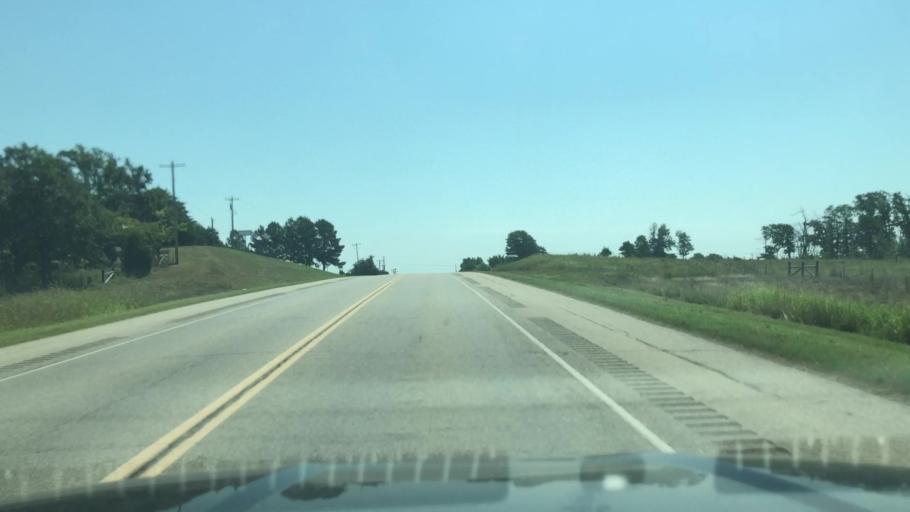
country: US
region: Oklahoma
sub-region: Creek County
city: Mannford
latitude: 36.0032
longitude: -96.4103
